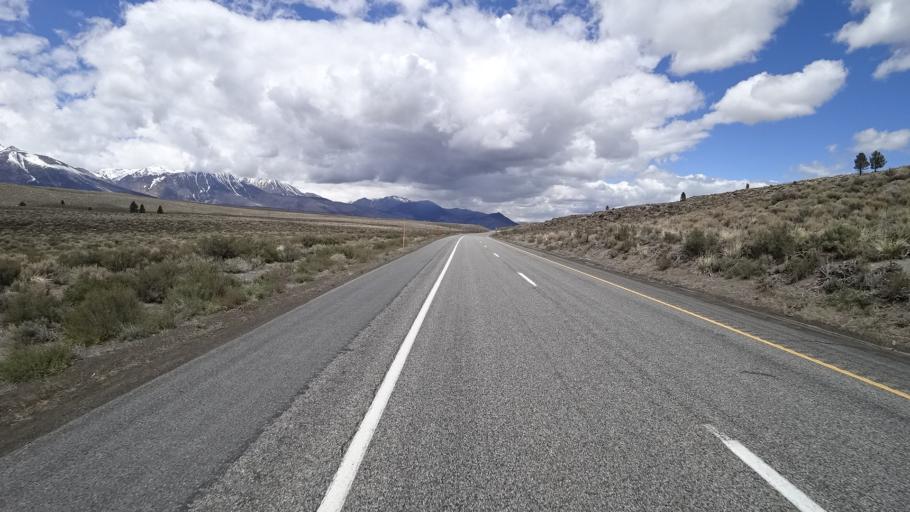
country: US
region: California
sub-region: Mono County
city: Mammoth Lakes
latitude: 37.8404
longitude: -119.0768
